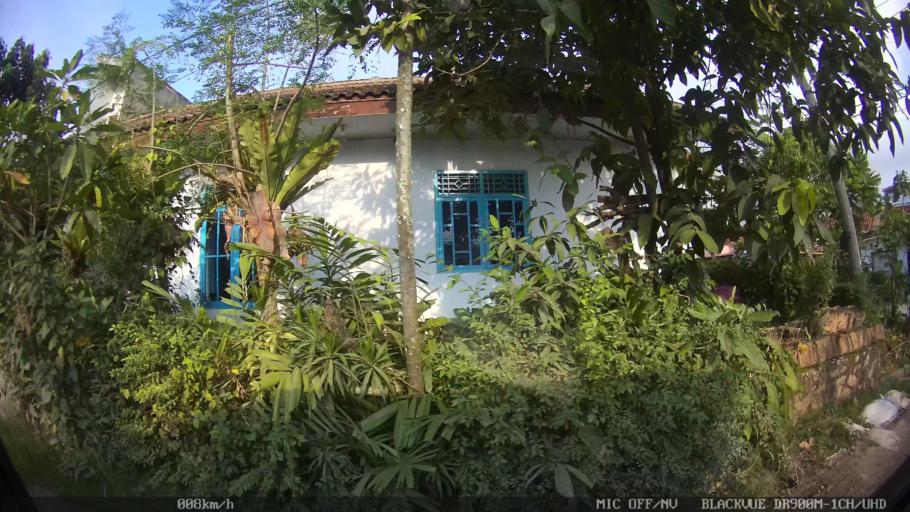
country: ID
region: Lampung
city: Kedaton
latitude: -5.4029
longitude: 105.3077
